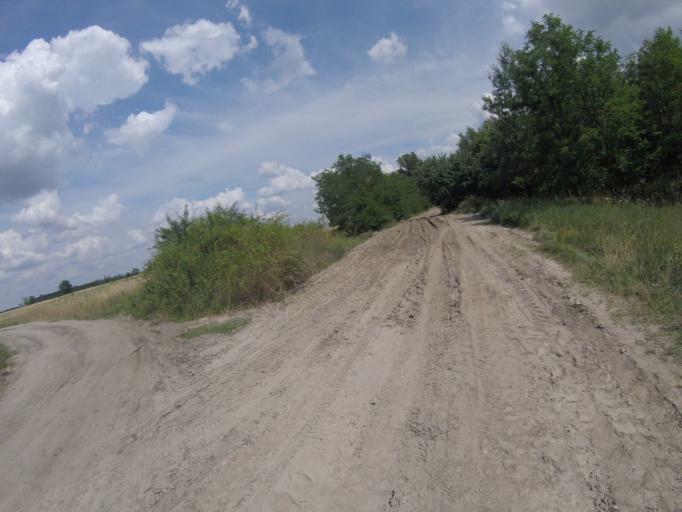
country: HU
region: Pest
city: Nagykoros
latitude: 47.0673
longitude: 19.7755
